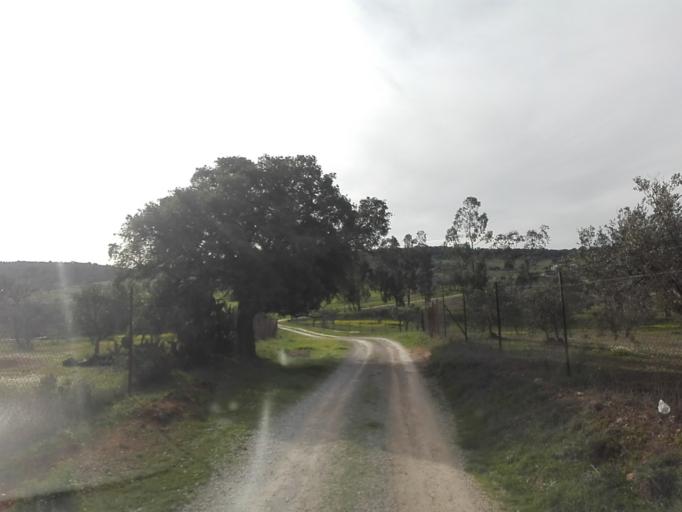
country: ES
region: Extremadura
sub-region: Provincia de Badajoz
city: Llerena
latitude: 38.2195
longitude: -6.0342
